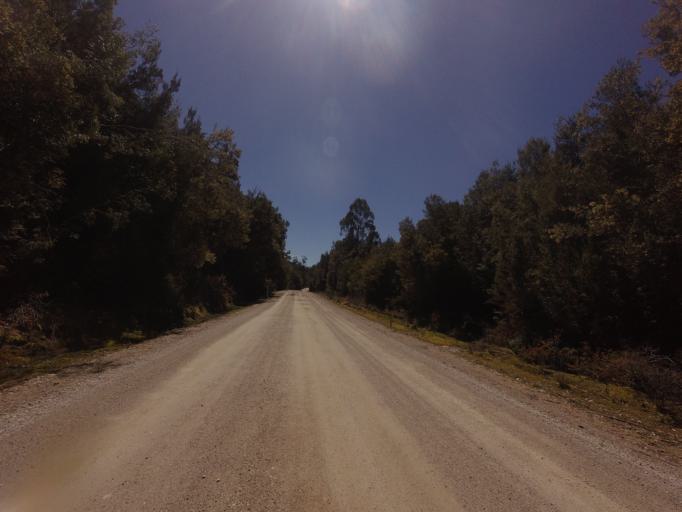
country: AU
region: Tasmania
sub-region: Huon Valley
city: Geeveston
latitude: -42.8314
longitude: 146.3854
